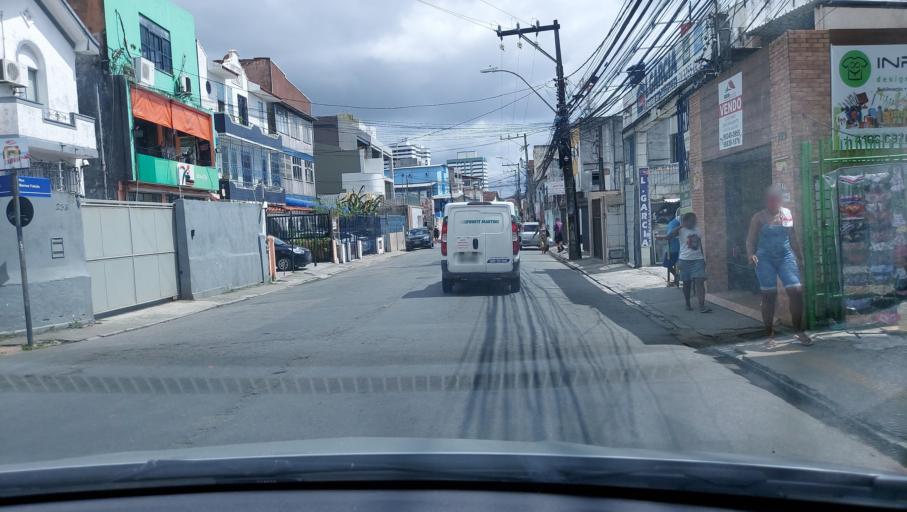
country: BR
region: Bahia
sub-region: Salvador
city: Salvador
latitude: -12.9752
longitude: -38.4944
